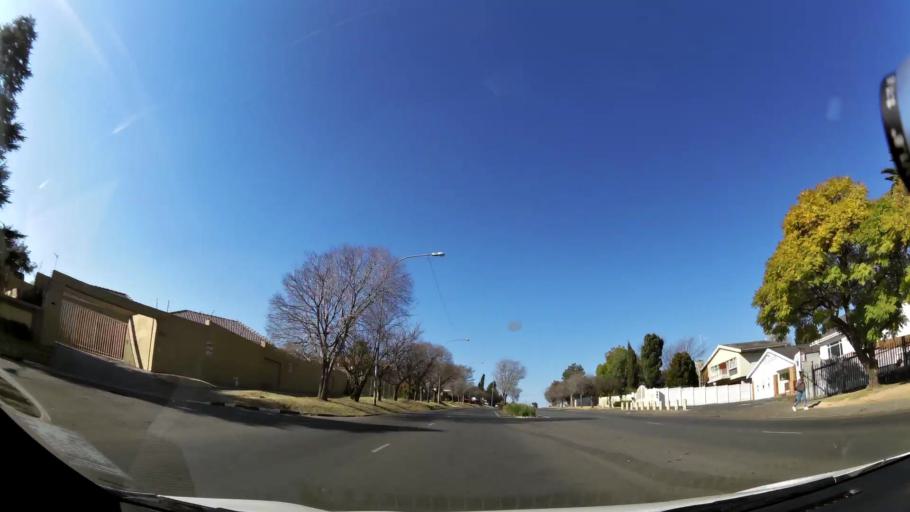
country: ZA
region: Gauteng
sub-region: City of Johannesburg Metropolitan Municipality
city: Johannesburg
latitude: -26.2734
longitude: 28.0151
